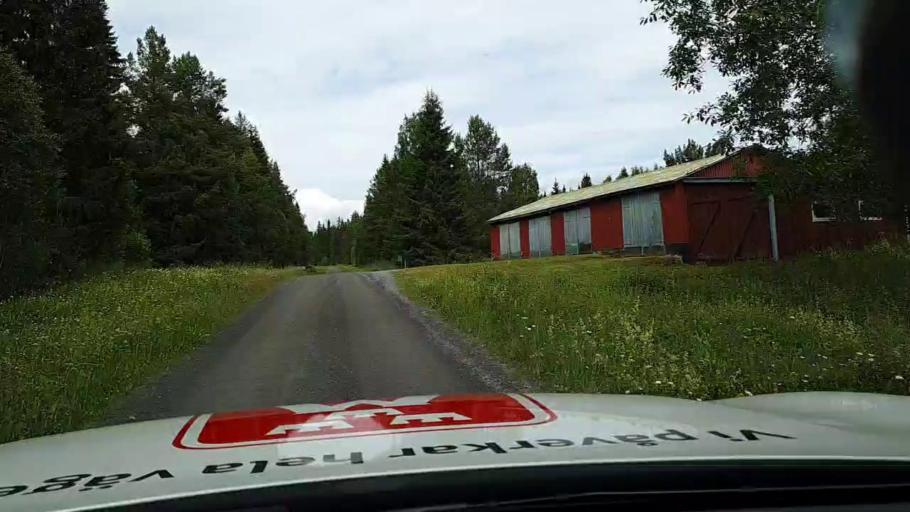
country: SE
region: Jaemtland
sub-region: OEstersunds Kommun
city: Lit
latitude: 63.2862
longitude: 15.2420
